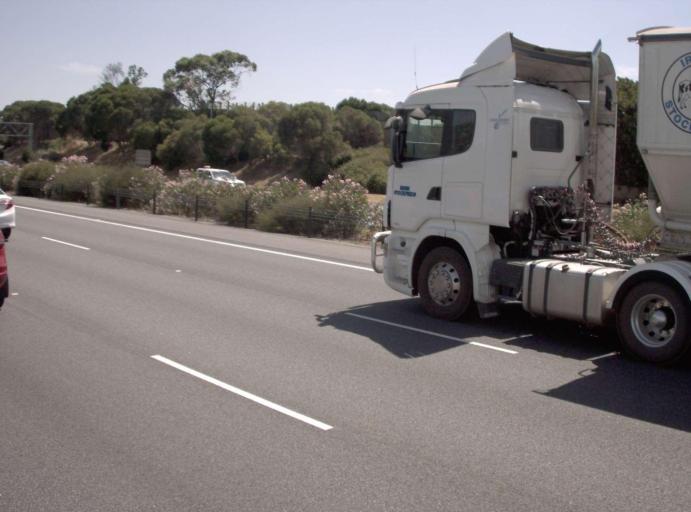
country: AU
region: Victoria
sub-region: Monash
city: Mulgrave
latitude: -37.9185
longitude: 145.1715
